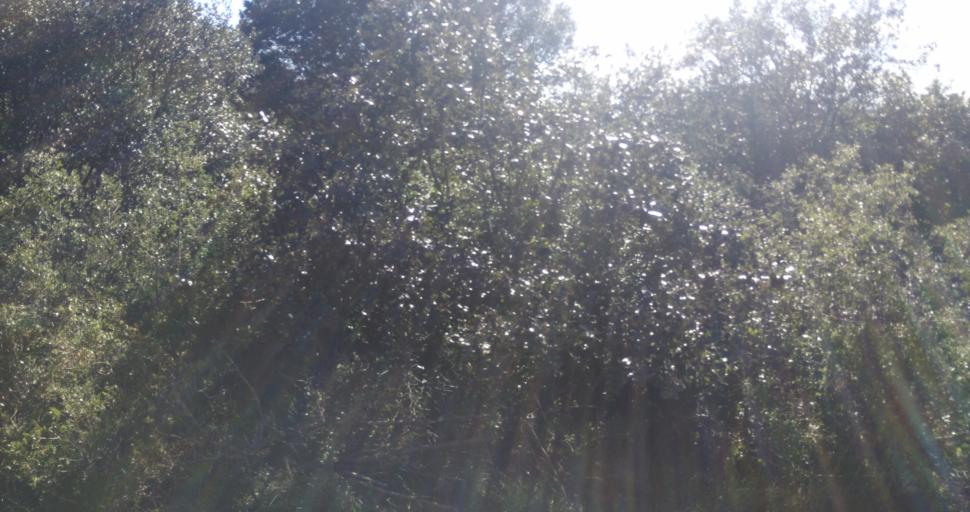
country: FR
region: Languedoc-Roussillon
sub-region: Departement du Gard
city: Calvisson
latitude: 43.8256
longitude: 4.1663
